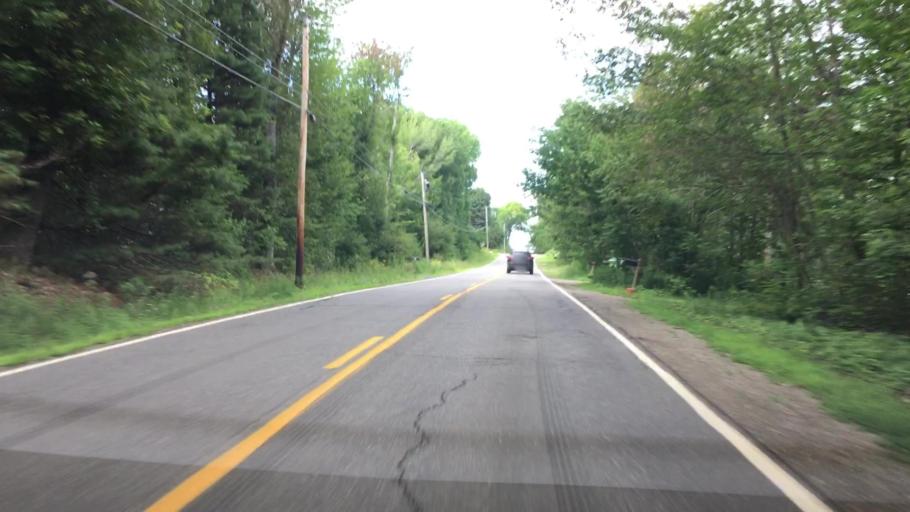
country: US
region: Maine
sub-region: Waldo County
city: Belfast
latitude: 44.3652
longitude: -69.0415
